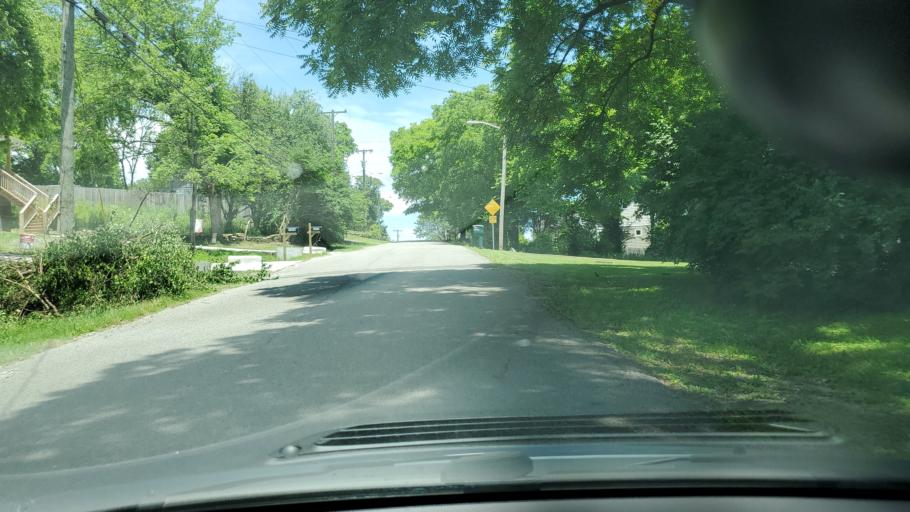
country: US
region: Tennessee
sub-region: Davidson County
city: Nashville
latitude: 36.2207
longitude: -86.7404
